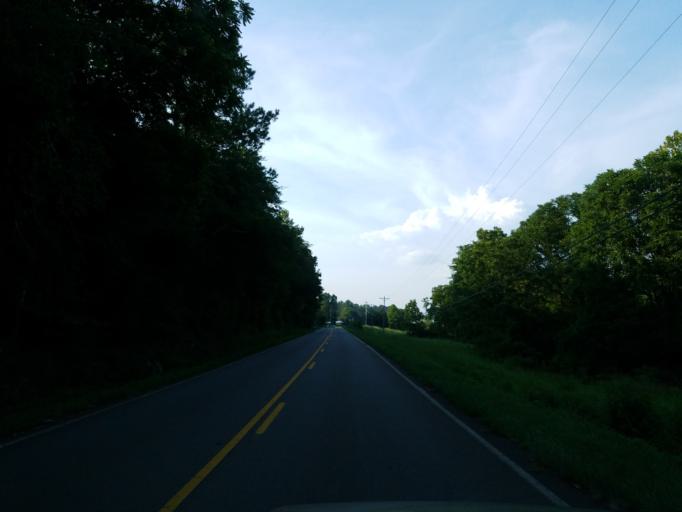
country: US
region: Georgia
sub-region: Pickens County
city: Jasper
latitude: 34.5574
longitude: -84.5391
